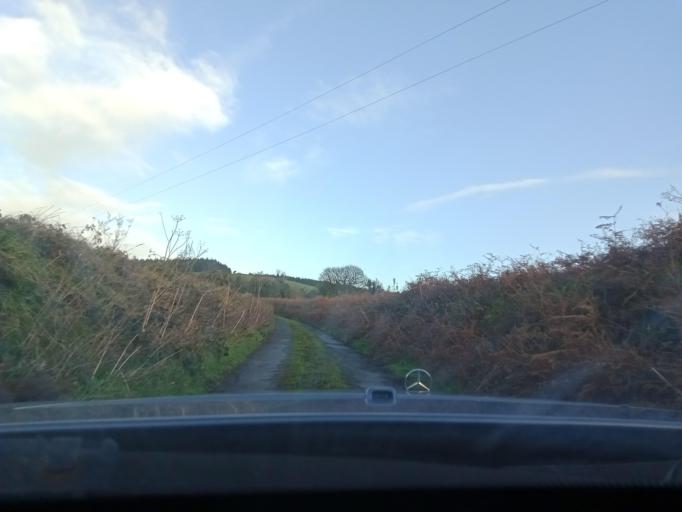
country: IE
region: Leinster
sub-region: Kilkenny
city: Callan
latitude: 52.4588
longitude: -7.4303
